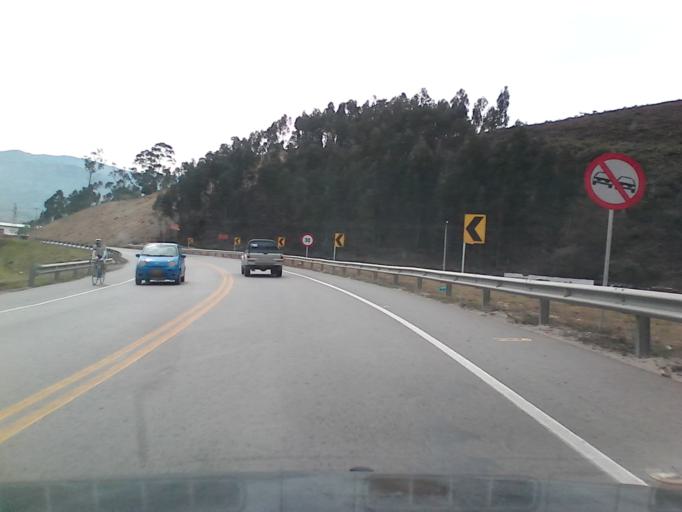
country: CO
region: Boyaca
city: Sogamoso
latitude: 5.7292
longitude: -72.9530
